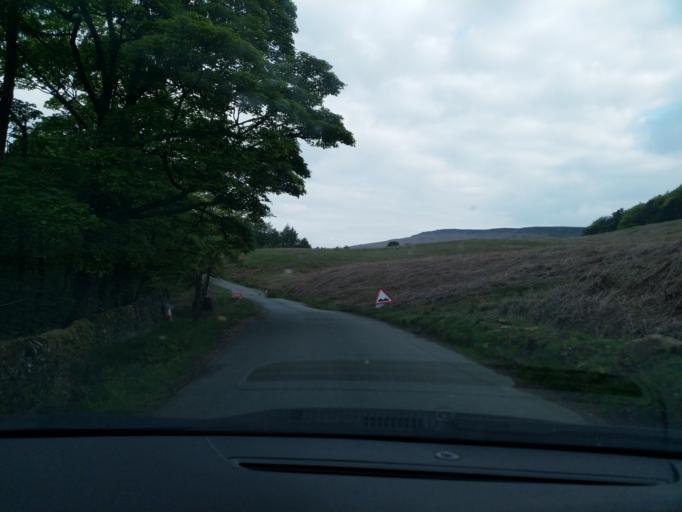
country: GB
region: England
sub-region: Derbyshire
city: Hathersage
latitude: 53.3487
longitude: -1.6405
